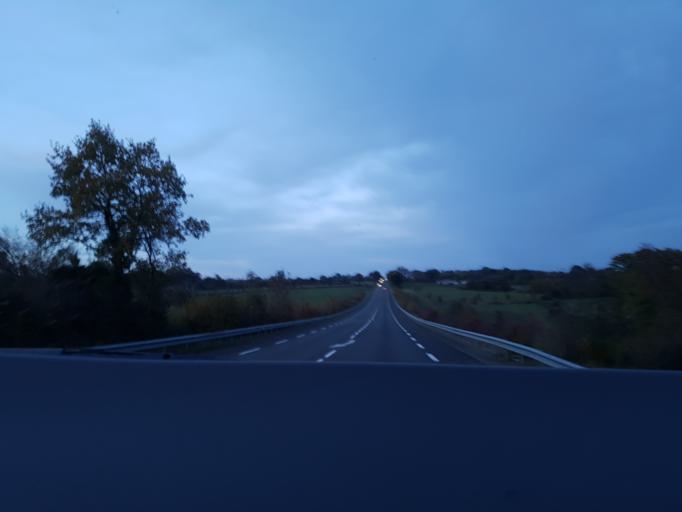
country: FR
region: Pays de la Loire
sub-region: Departement de la Mayenne
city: Montigne-le-Brillant
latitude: 48.0074
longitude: -0.8346
